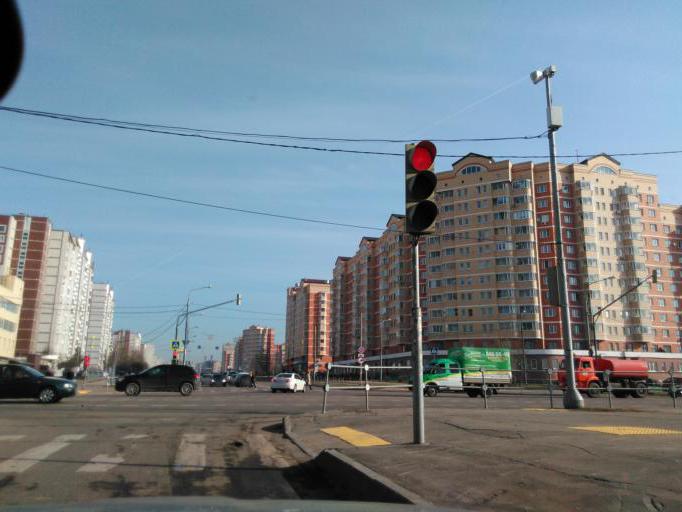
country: RU
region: Moscow
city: Zelenograd
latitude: 55.9698
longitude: 37.1619
